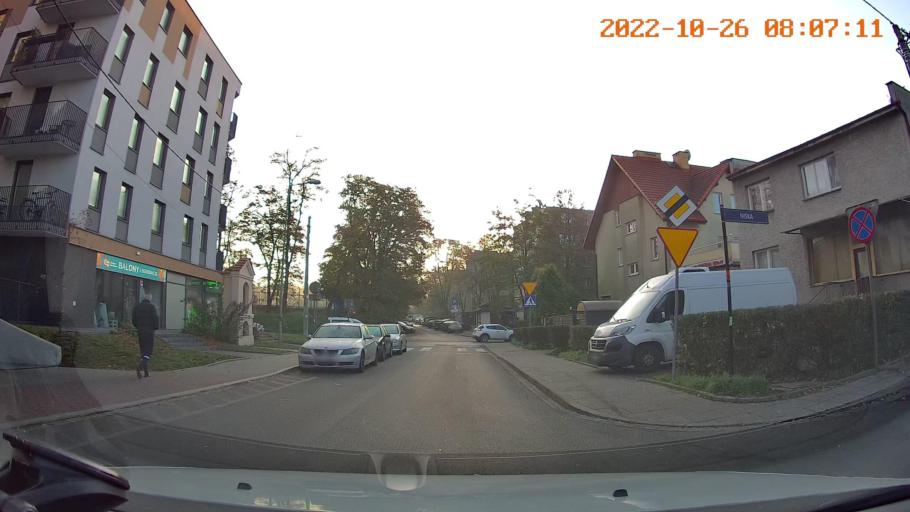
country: PL
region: Lesser Poland Voivodeship
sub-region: Krakow
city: Krakow
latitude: 50.0856
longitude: 19.9159
